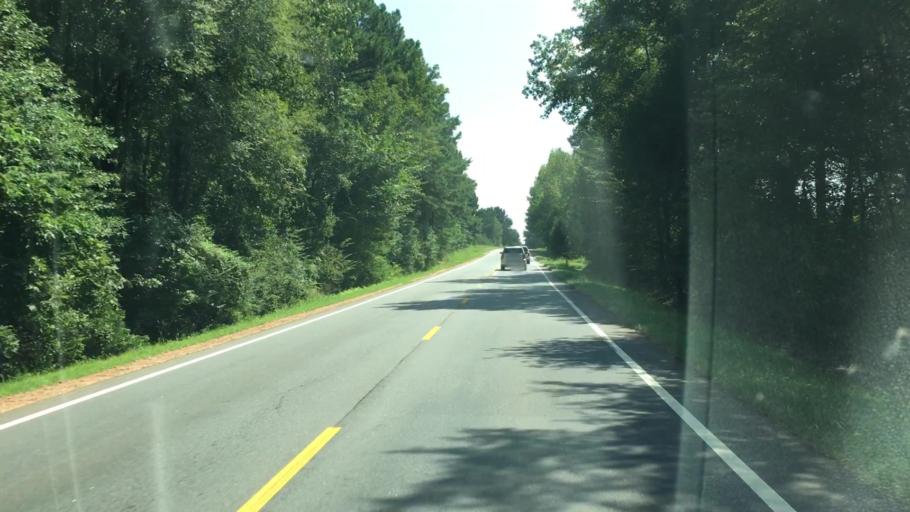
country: US
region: Georgia
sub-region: Oconee County
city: Watkinsville
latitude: 33.7876
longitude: -83.4237
